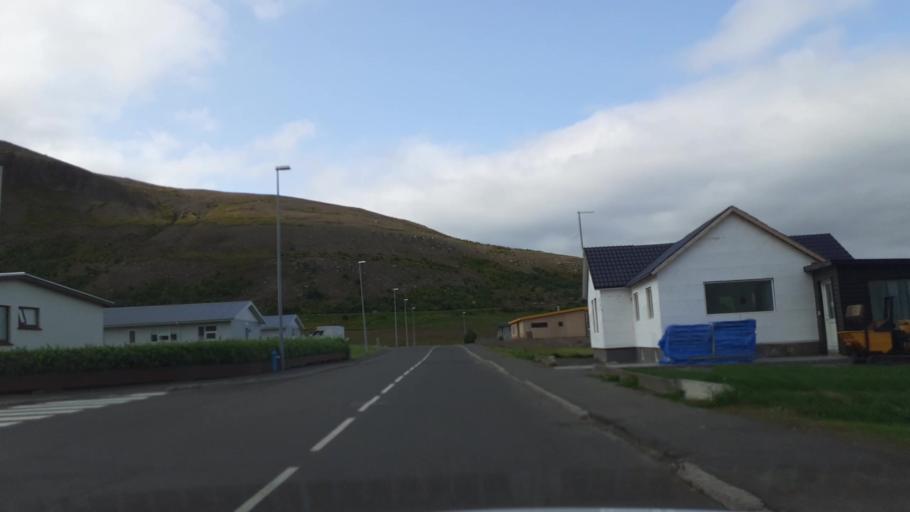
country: IS
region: Northeast
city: Akureyri
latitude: 65.9462
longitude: -18.1860
